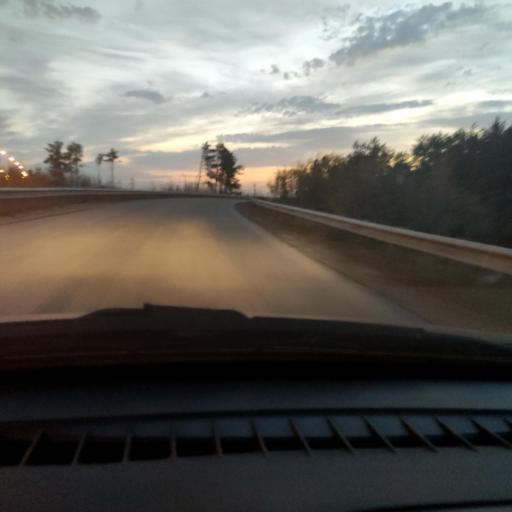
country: RU
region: Samara
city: Zhigulevsk
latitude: 53.5203
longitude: 49.5386
